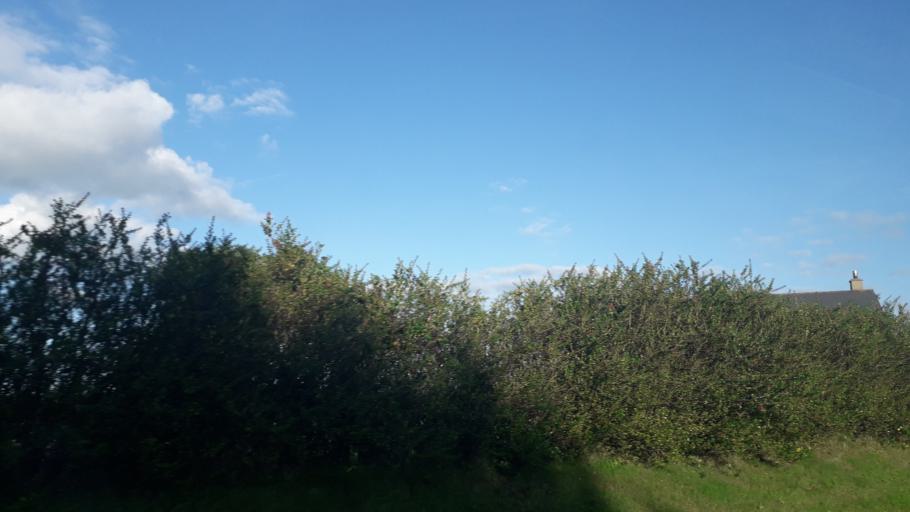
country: IE
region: Leinster
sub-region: Lu
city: Carlingford
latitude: 54.0291
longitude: -6.1565
